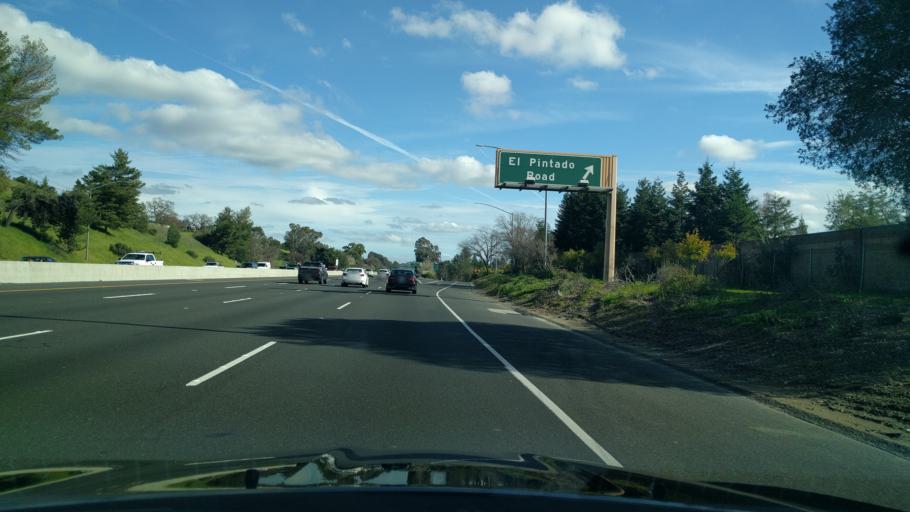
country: US
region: California
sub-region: Contra Costa County
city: Danville
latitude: 37.8367
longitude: -122.0125
